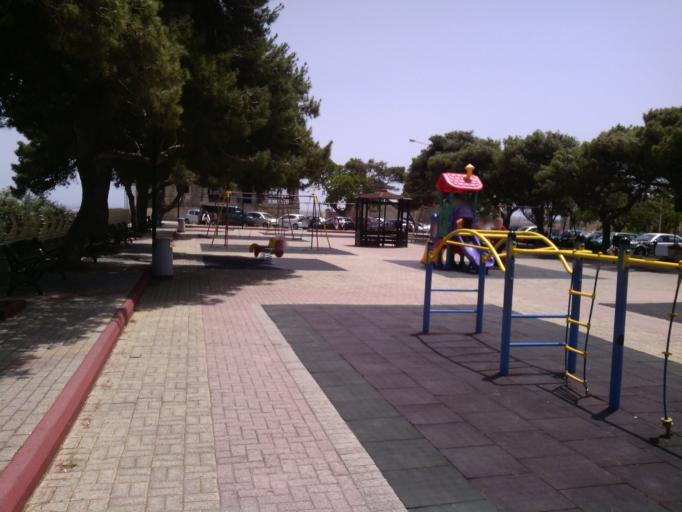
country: MT
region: L-Imdina
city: Imdina
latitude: 35.8843
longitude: 14.4036
